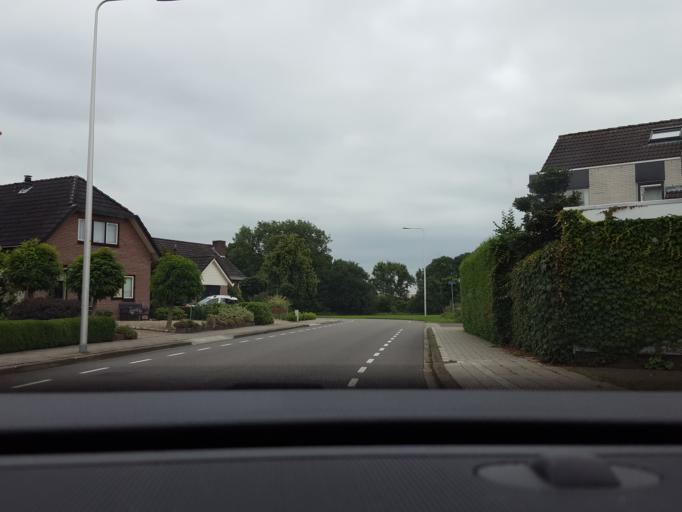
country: NL
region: Gelderland
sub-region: Gemeente Brummen
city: Brummen
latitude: 52.0833
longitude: 6.1499
